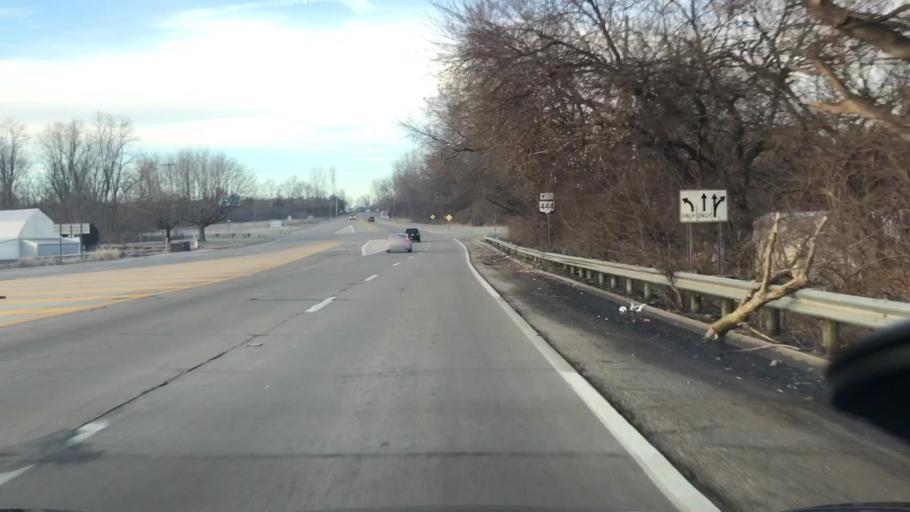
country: US
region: Ohio
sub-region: Clark County
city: Holiday Valley
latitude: 39.8447
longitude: -83.9949
